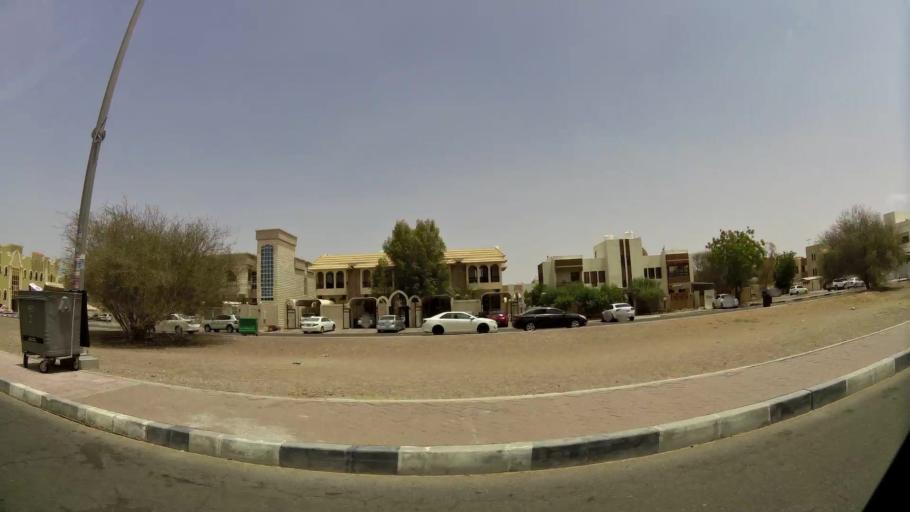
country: AE
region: Abu Dhabi
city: Al Ain
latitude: 24.2067
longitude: 55.7143
